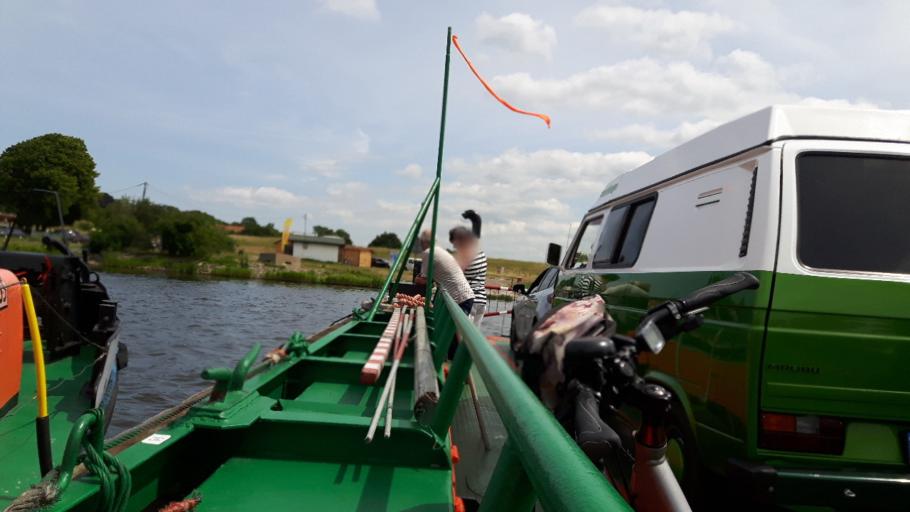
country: PL
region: Pomeranian Voivodeship
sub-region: Powiat nowodworski
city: Ostaszewo
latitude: 54.3328
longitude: 18.9420
